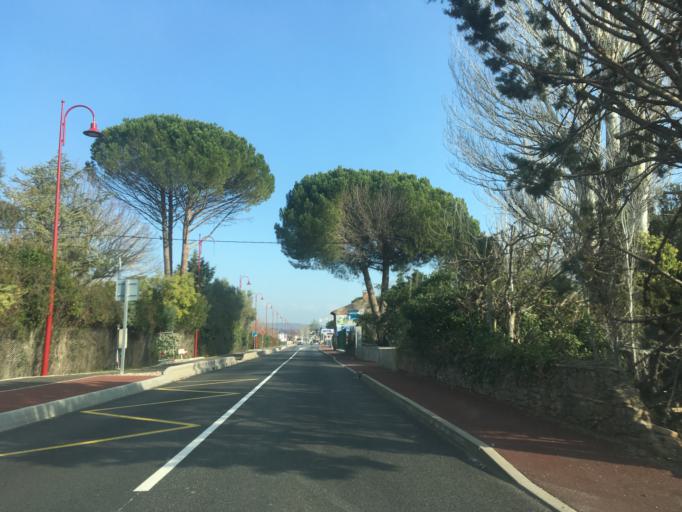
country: FR
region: Provence-Alpes-Cote d'Azur
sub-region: Departement du Var
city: Vidauban
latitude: 43.4178
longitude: 6.4222
